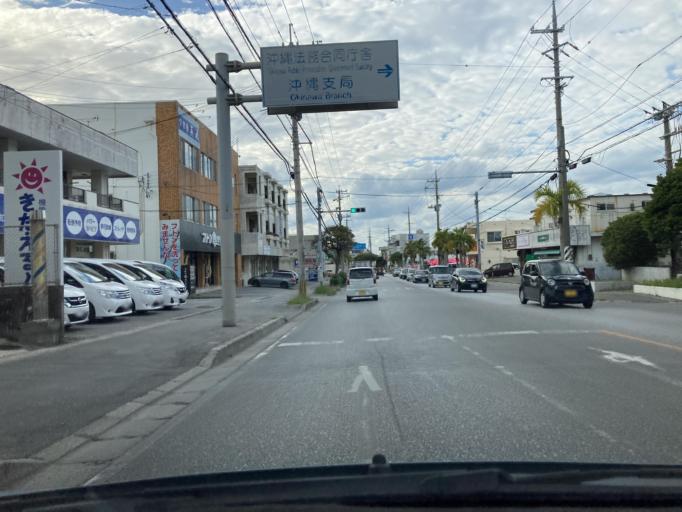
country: JP
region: Okinawa
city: Okinawa
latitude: 26.3603
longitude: 127.8200
